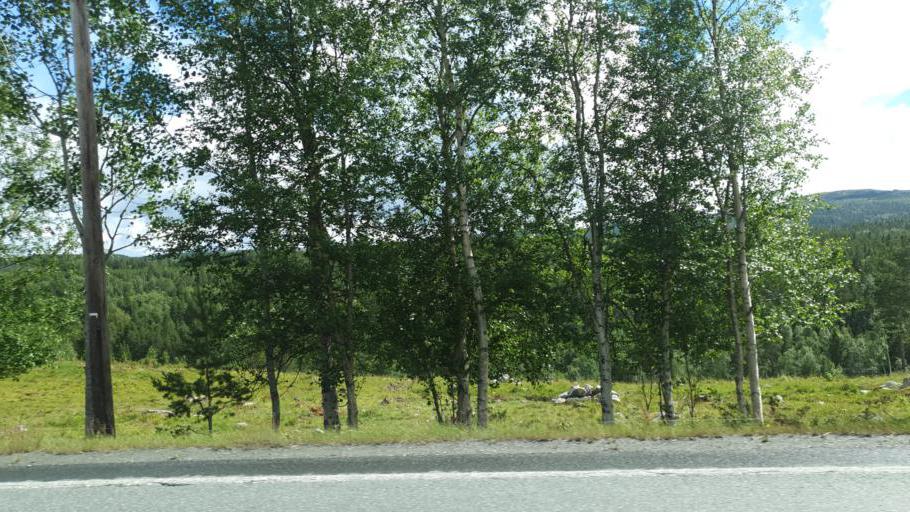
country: NO
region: Sor-Trondelag
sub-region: Rennebu
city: Berkak
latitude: 62.7005
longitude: 9.9474
